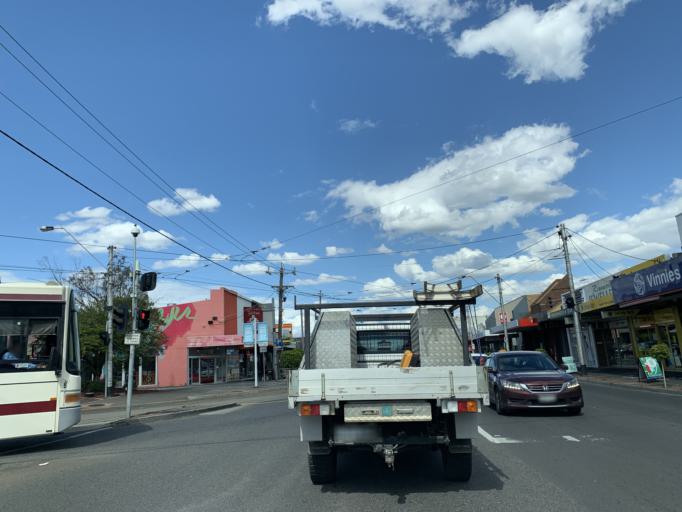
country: AU
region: Victoria
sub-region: Moonee Valley
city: Niddrie
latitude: -37.7360
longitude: 144.8891
